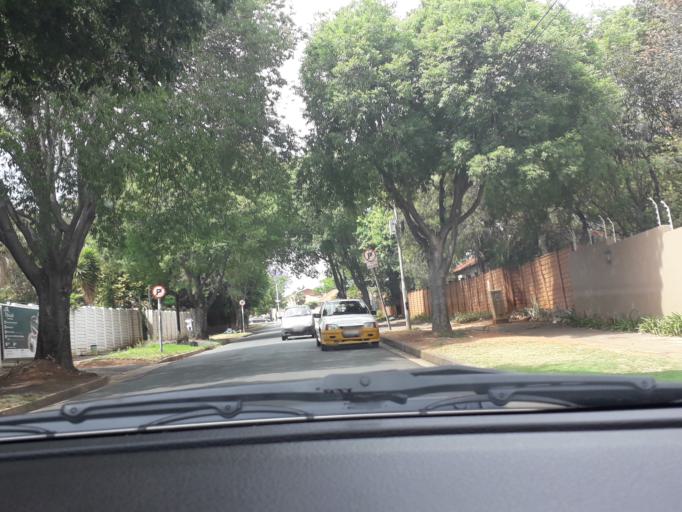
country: ZA
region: Gauteng
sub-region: City of Johannesburg Metropolitan Municipality
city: Johannesburg
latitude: -26.1386
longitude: 28.0853
